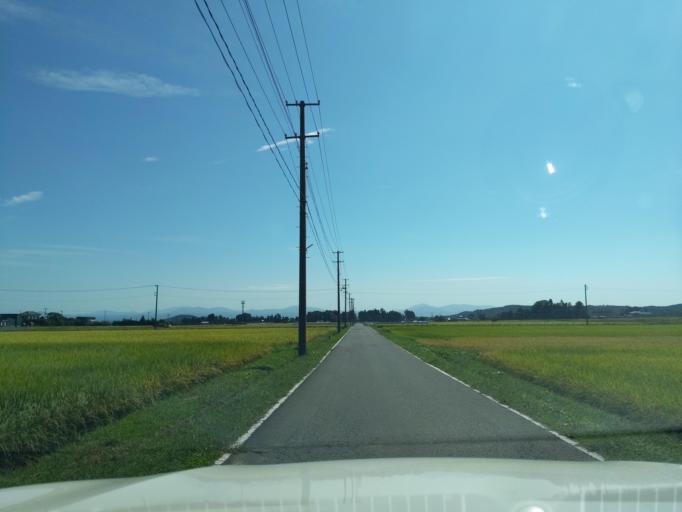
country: JP
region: Fukushima
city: Koriyama
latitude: 37.4024
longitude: 140.2585
